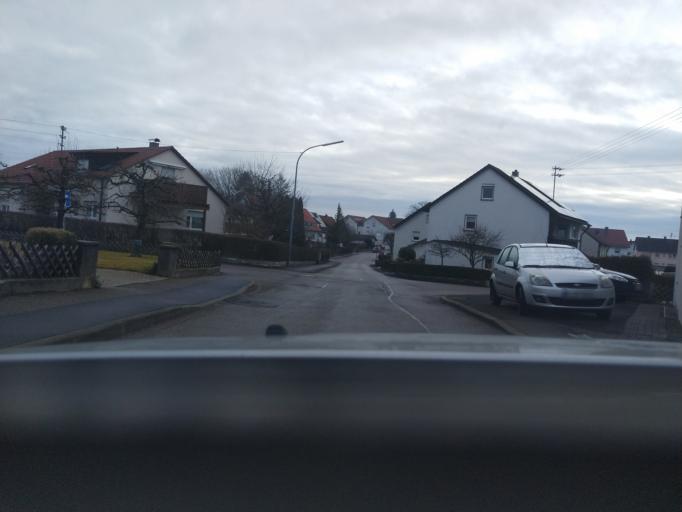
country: DE
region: Baden-Wuerttemberg
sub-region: Regierungsbezirk Stuttgart
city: Durlangen
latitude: 48.8594
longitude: 9.7922
